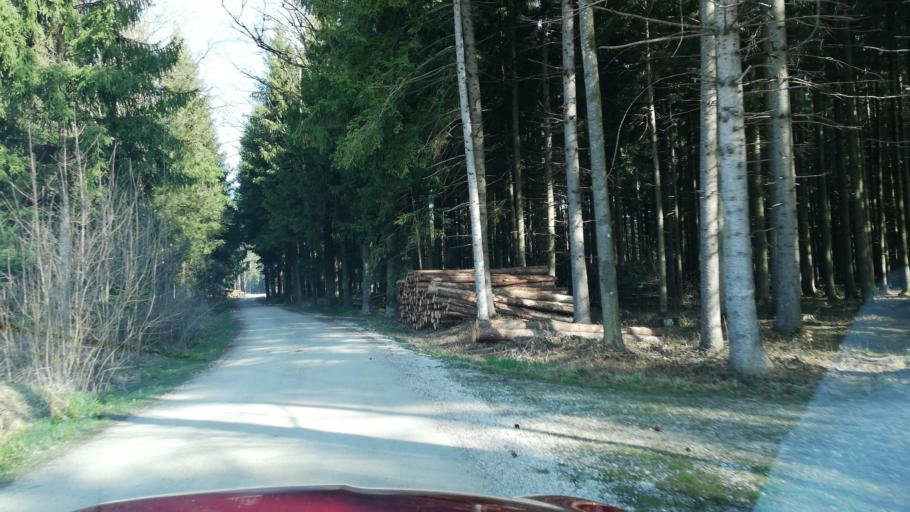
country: AT
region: Upper Austria
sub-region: Politischer Bezirk Kirchdorf an der Krems
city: Kremsmunster
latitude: 48.0816
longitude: 14.1169
